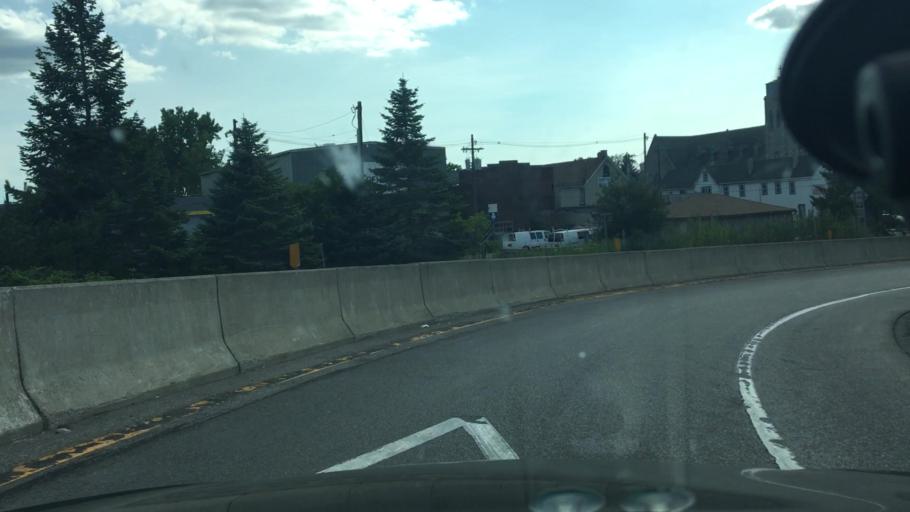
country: US
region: New York
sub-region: Erie County
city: Buffalo
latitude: 42.8692
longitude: -78.8447
